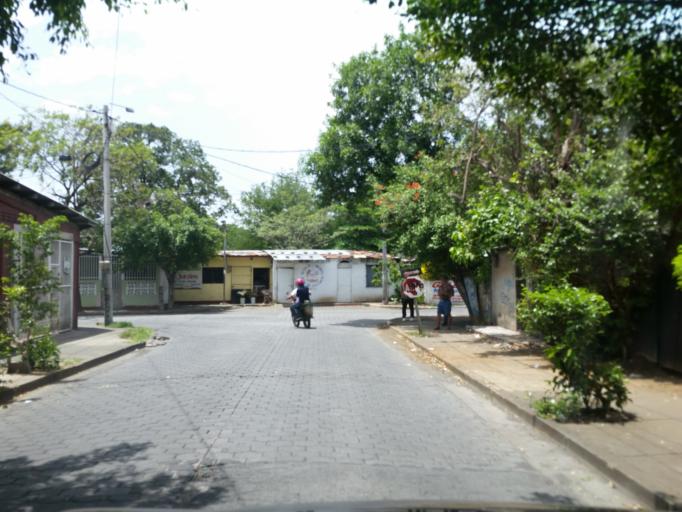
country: NI
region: Managua
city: Managua
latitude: 12.1399
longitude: -86.2469
